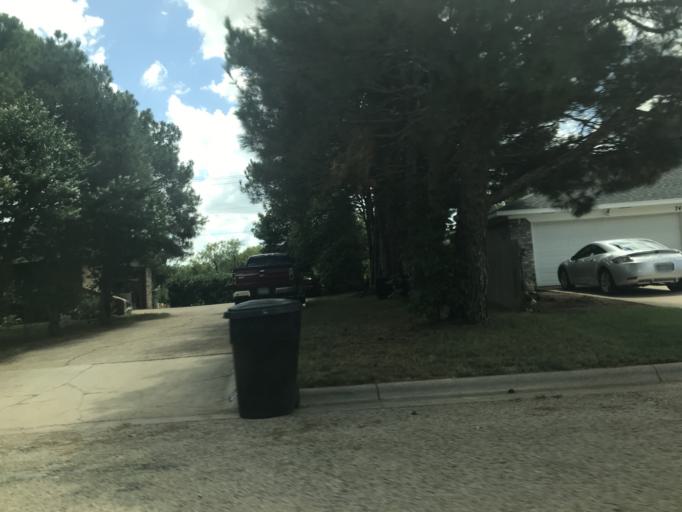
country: US
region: Texas
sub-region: Taylor County
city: Abilene
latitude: 32.4417
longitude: -99.6978
